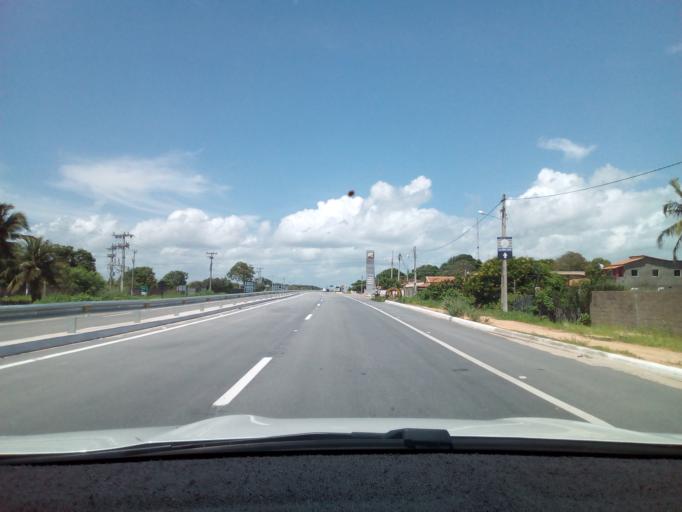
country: BR
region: Ceara
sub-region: Aracati
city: Aracati
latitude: -4.4715
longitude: -37.8012
